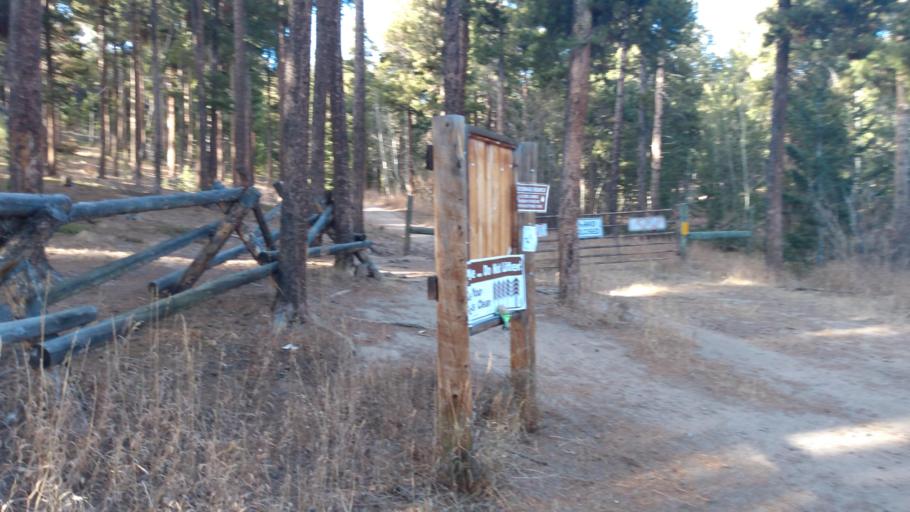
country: US
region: Colorado
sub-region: Boulder County
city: Nederland
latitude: 39.9573
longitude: -105.4473
